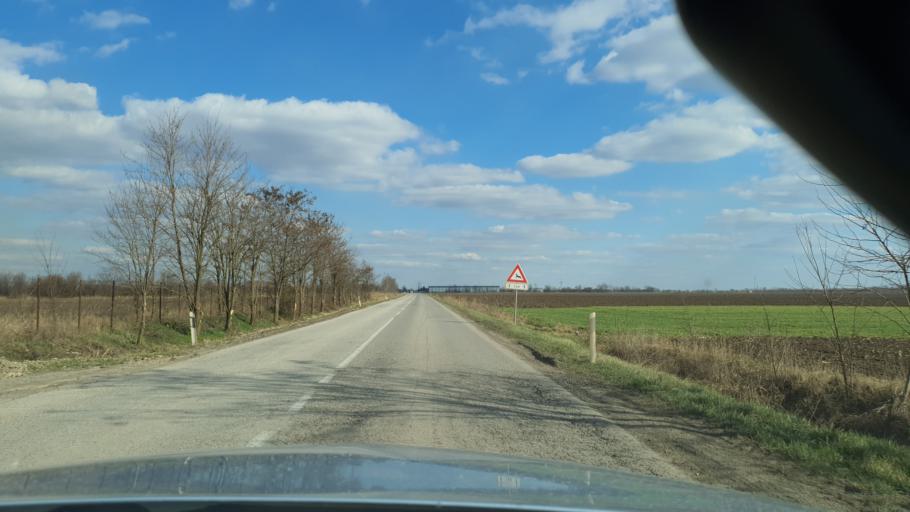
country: RS
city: Zmajevo
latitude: 45.4473
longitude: 19.7044
